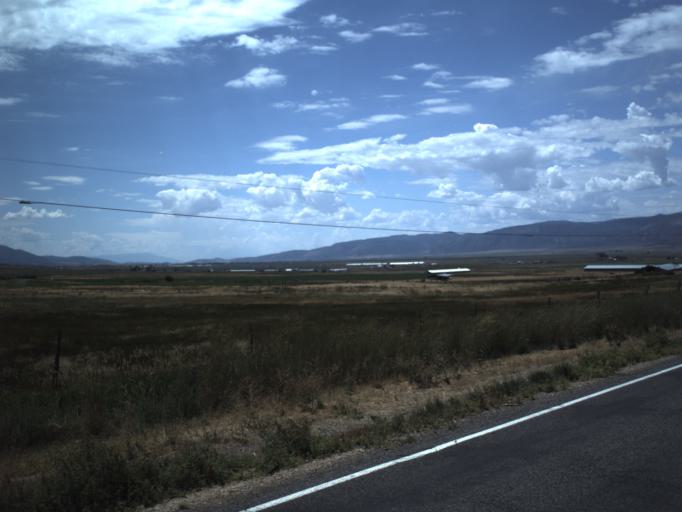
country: US
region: Utah
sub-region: Sanpete County
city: Moroni
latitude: 39.4807
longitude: -111.5322
